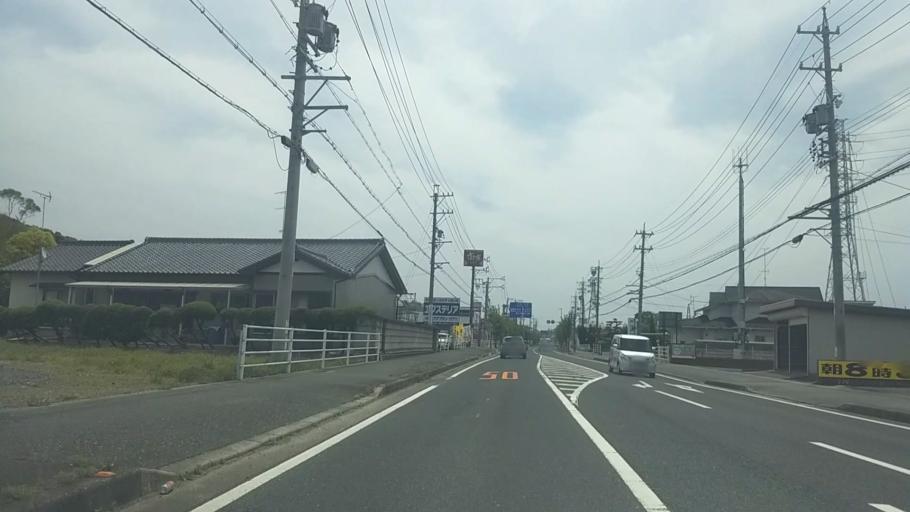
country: JP
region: Shizuoka
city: Kosai-shi
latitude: 34.7182
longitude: 137.5336
